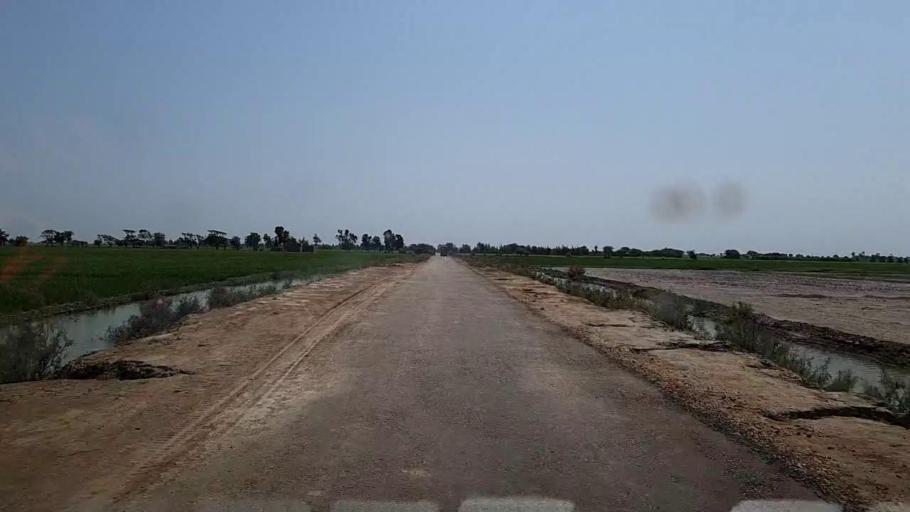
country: PK
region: Sindh
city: Mirpur Batoro
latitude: 24.6195
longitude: 68.4522
